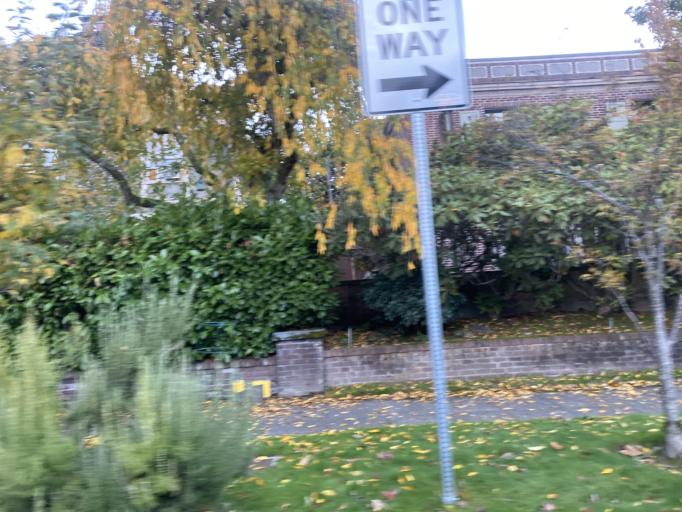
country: US
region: Washington
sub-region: King County
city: Seattle
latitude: 47.6461
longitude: -122.3016
